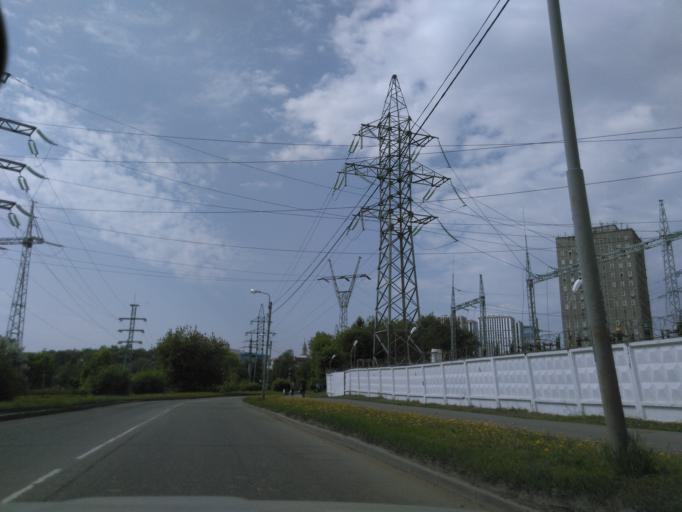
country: RU
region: Moscow
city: Golovinskiy
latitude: 55.8457
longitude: 37.5046
